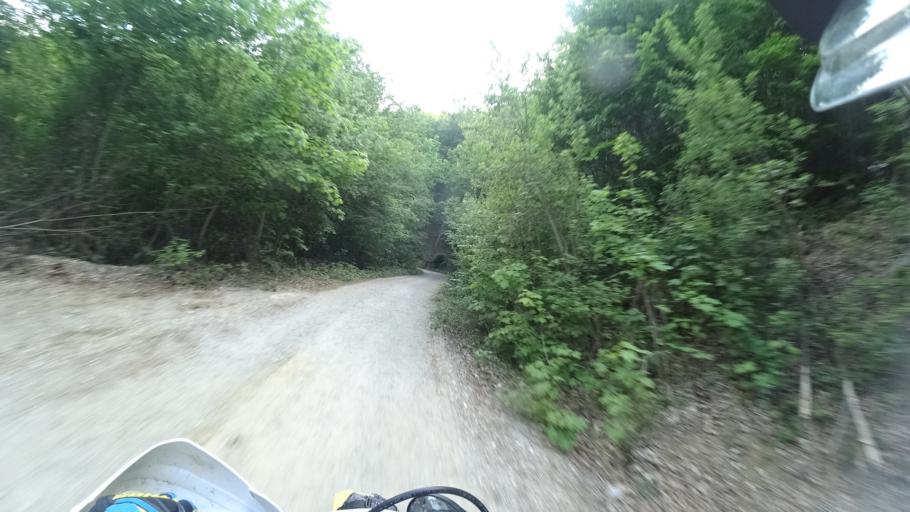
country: HR
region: Zagrebacka
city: Jablanovec
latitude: 45.8590
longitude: 15.8899
